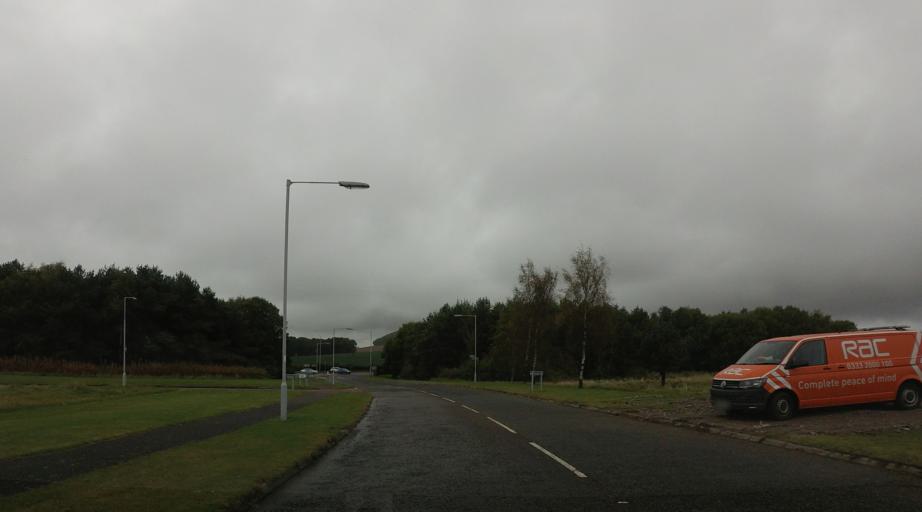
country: GB
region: Scotland
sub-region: Fife
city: Newport-On-Tay
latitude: 56.4157
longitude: -2.9153
